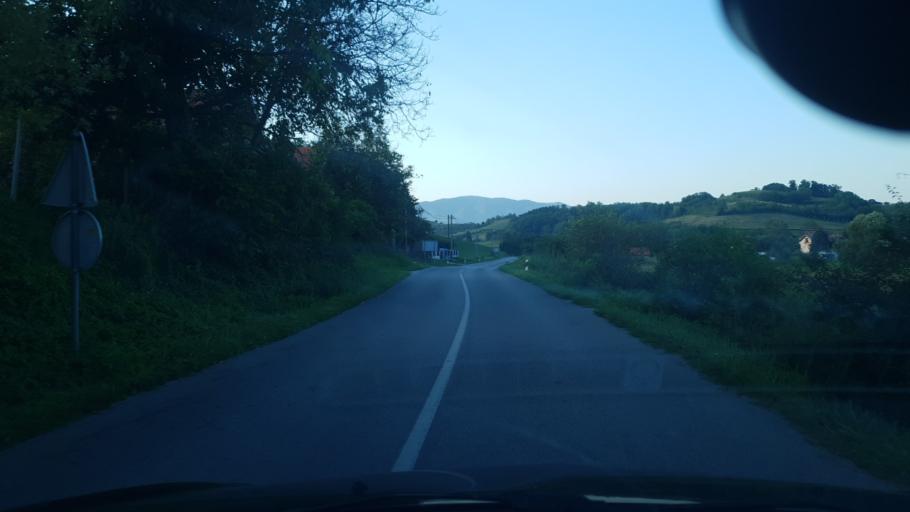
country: HR
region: Krapinsko-Zagorska
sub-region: Grad Krapina
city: Krapina
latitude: 46.1104
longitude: 15.8728
